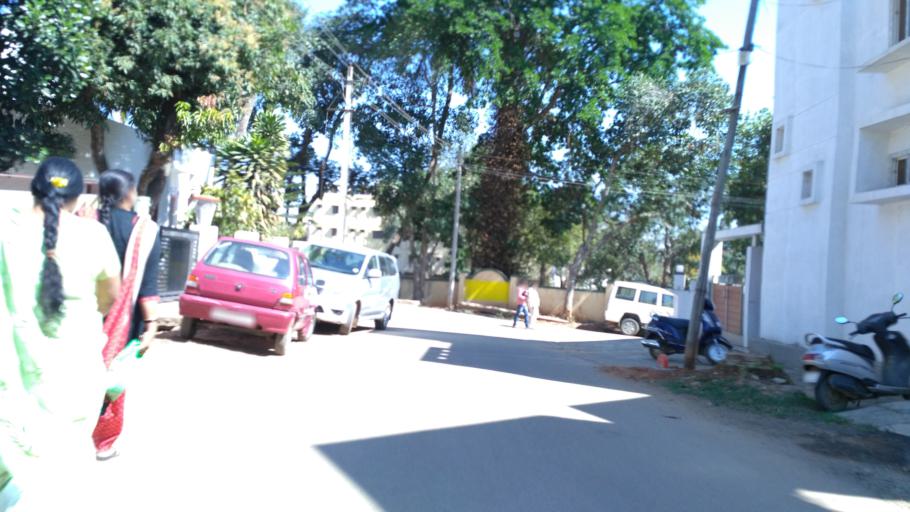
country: IN
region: Karnataka
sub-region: Hassan
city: Hassan
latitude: 13.0042
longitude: 76.1082
